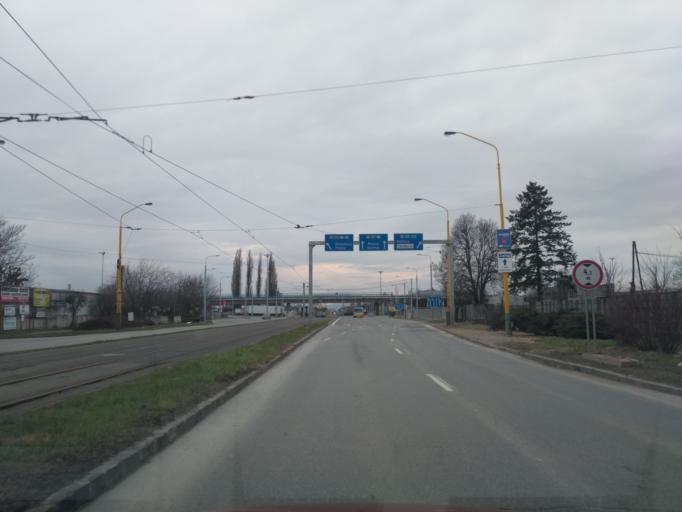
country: SK
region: Kosicky
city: Kosice
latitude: 48.6909
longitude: 21.2654
